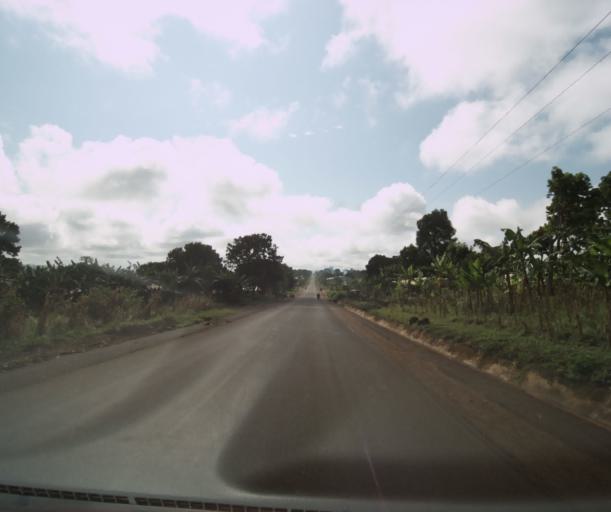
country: CM
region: West
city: Bafoussam
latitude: 5.4834
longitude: 10.4727
